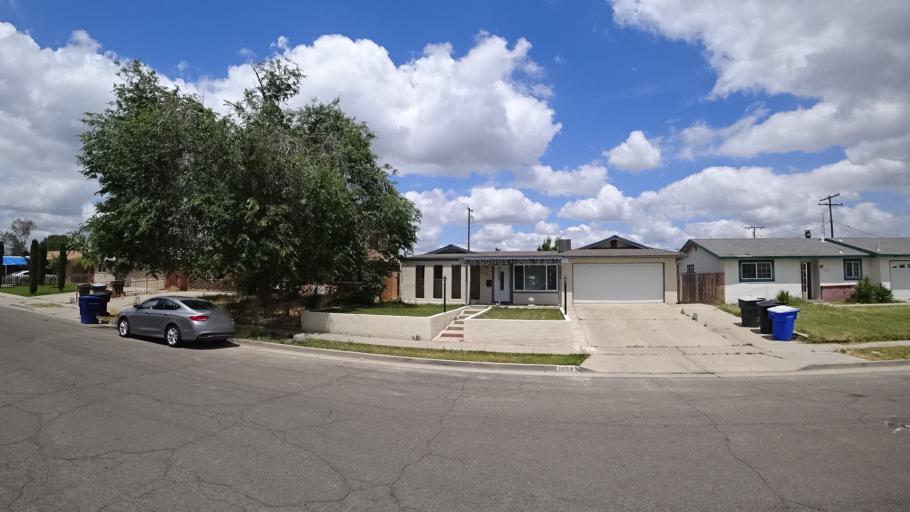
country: US
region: California
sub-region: Kings County
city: Hanford
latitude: 36.3114
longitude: -119.6721
